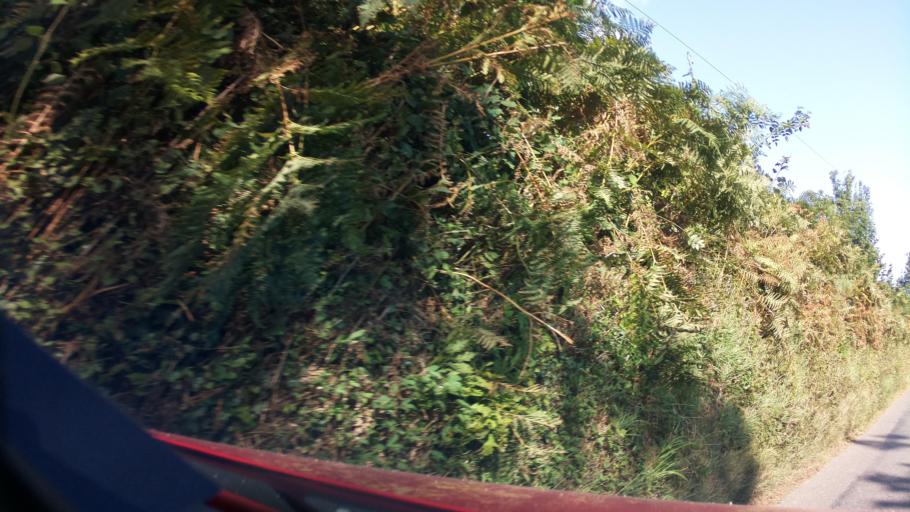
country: GB
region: England
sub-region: Devon
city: Ashburton
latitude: 50.5132
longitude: -3.7751
